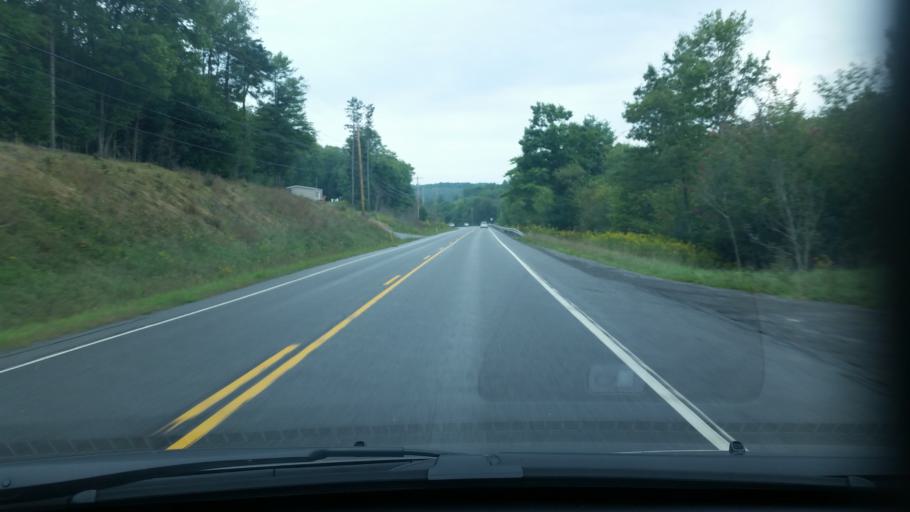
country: US
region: Pennsylvania
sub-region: Clearfield County
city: Shiloh
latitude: 41.0961
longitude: -78.2461
